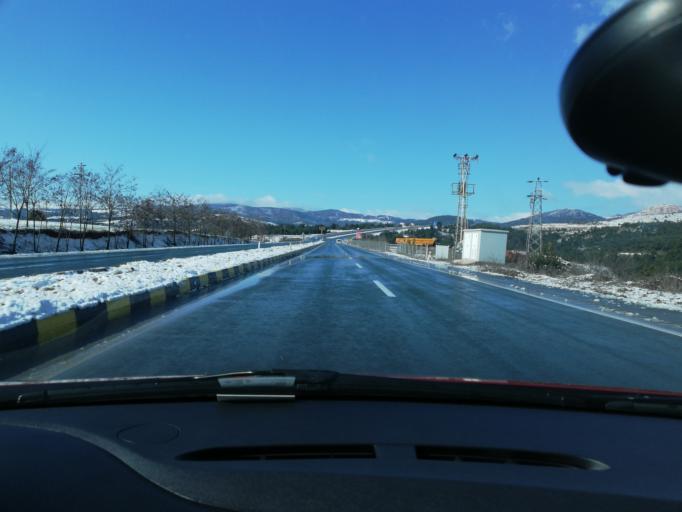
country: TR
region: Kastamonu
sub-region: Cide
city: Kastamonu
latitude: 41.3666
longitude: 33.7441
